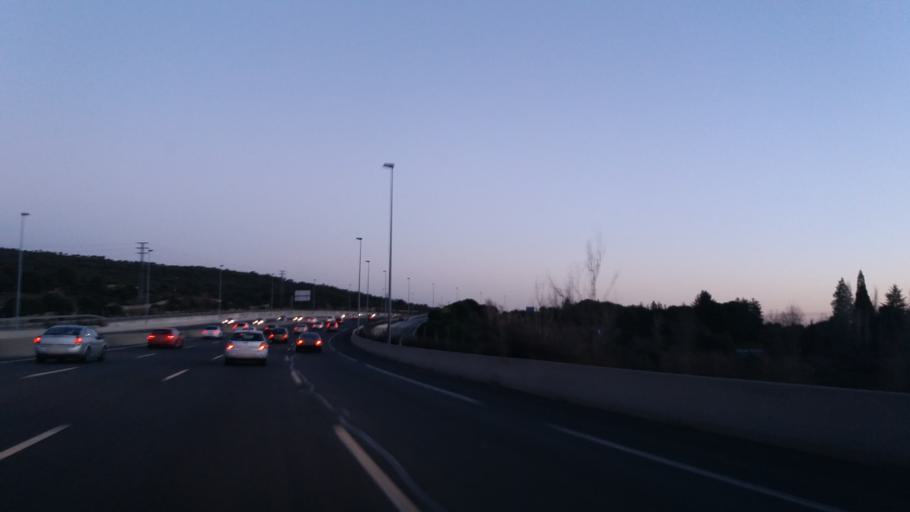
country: ES
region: Madrid
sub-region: Provincia de Madrid
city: Galapagar
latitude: 40.6044
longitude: -3.9675
